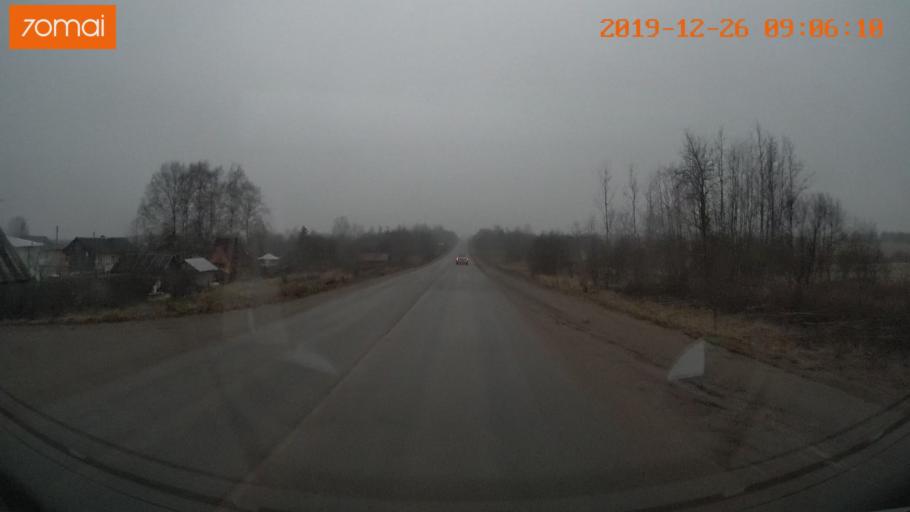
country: RU
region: Vologda
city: Gryazovets
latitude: 58.8332
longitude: 40.2545
